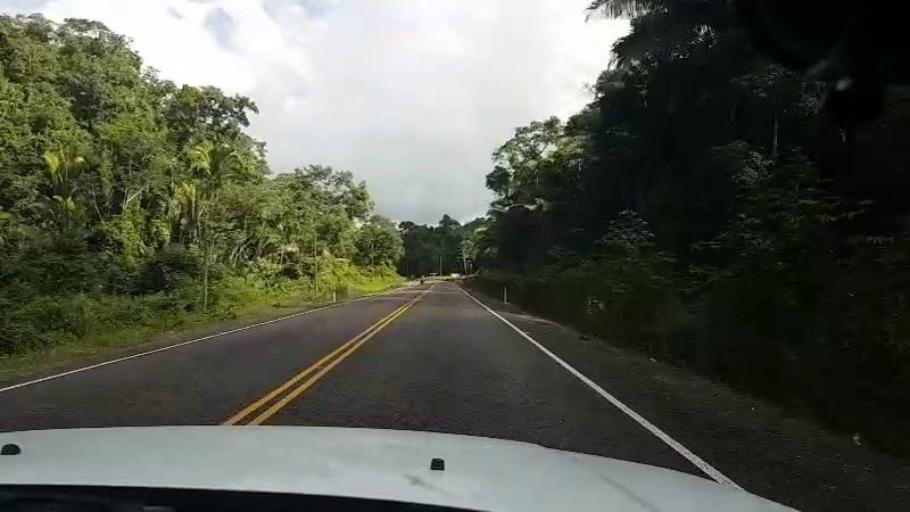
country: BZ
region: Cayo
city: Belmopan
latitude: 17.1497
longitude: -88.7154
